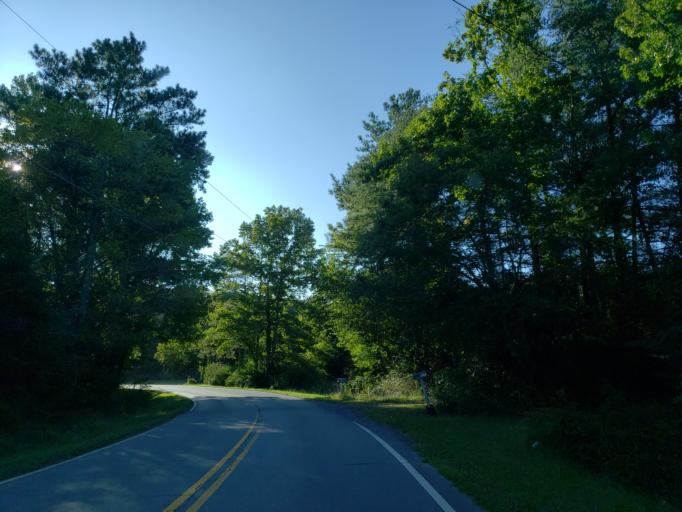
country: US
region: Georgia
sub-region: Bartow County
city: Rydal
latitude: 34.2816
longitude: -84.8070
